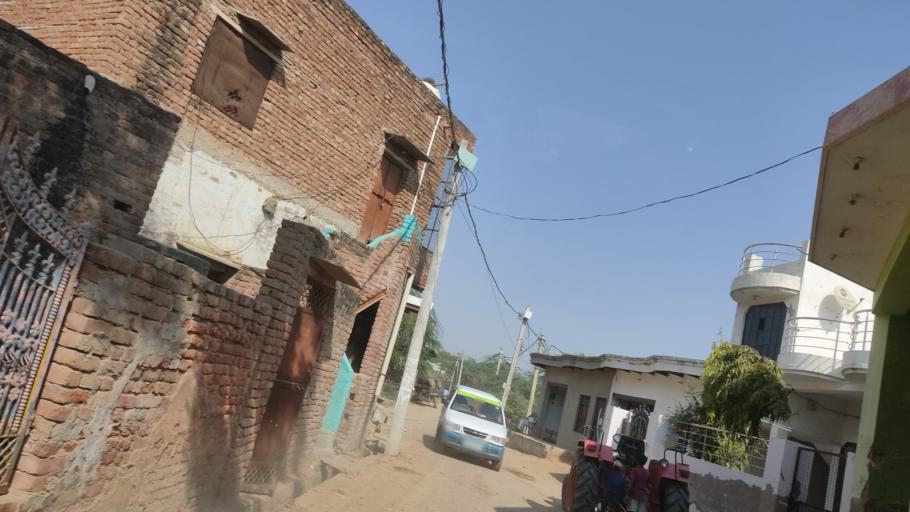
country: IN
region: Uttar Pradesh
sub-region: Mathura
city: Radha Kund
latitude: 27.5104
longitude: 77.4981
